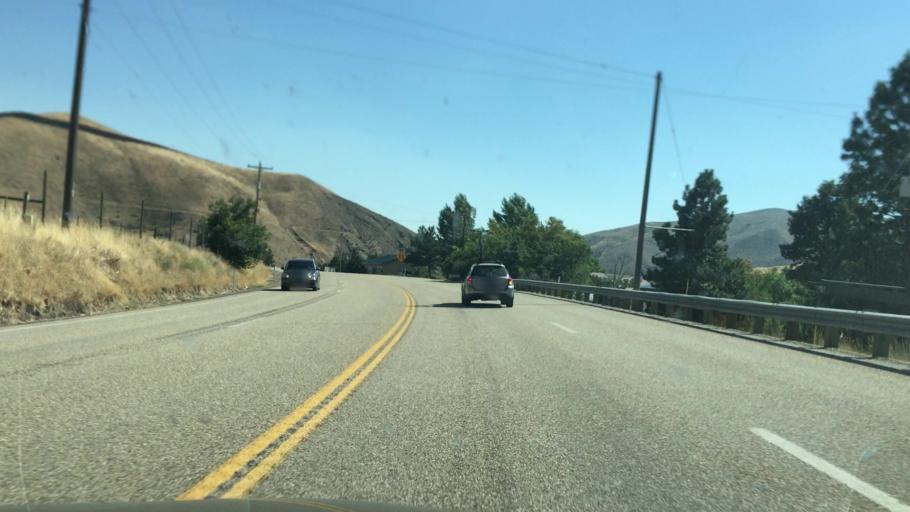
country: US
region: Idaho
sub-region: Gem County
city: Emmett
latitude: 43.9932
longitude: -116.1876
